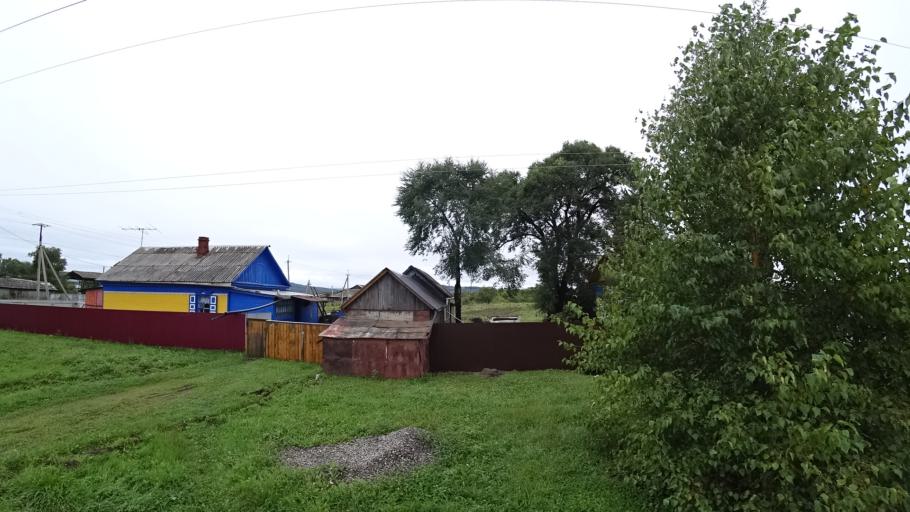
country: RU
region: Primorskiy
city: Monastyrishche
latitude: 44.2002
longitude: 132.4512
